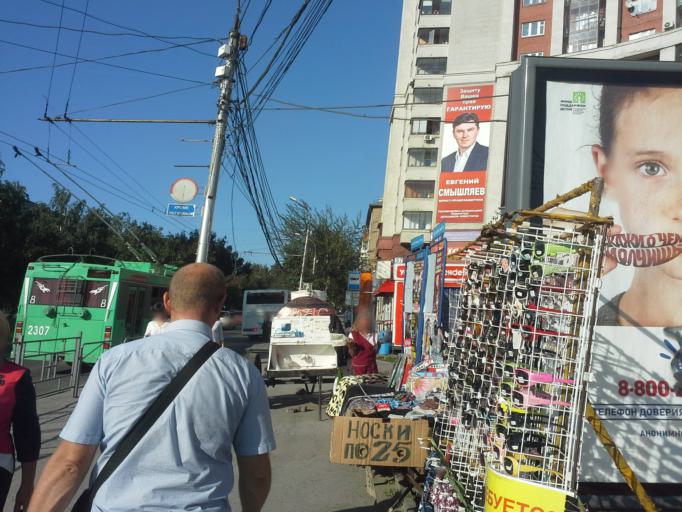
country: RU
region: Novosibirsk
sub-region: Novosibirskiy Rayon
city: Novosibirsk
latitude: 55.0105
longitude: 82.9394
